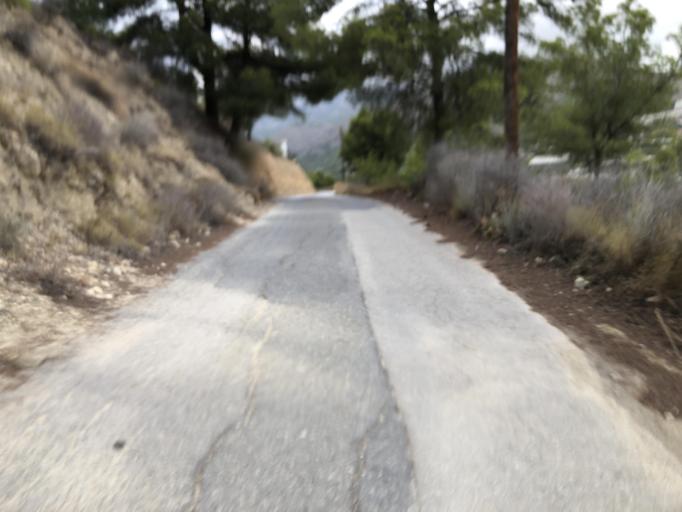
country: ES
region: Valencia
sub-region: Provincia de Alicante
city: Polop
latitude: 38.6368
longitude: -0.1326
